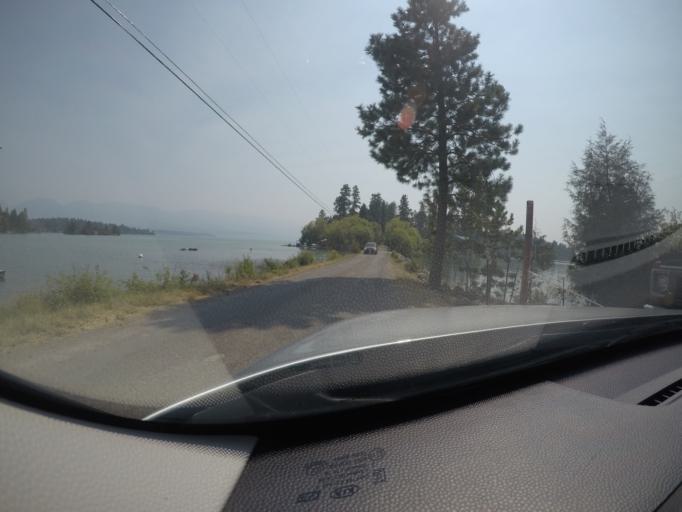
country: US
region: Montana
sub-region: Lake County
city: Polson
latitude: 47.7681
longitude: -114.1428
